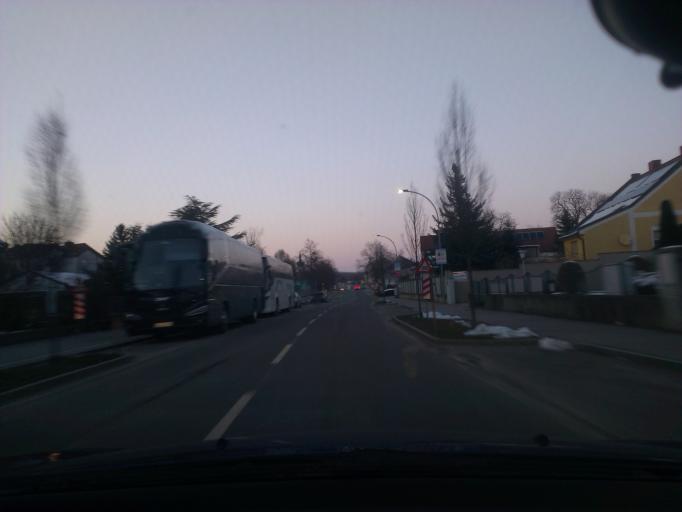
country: AT
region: Lower Austria
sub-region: Politischer Bezirk Wien-Umgebung
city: Fischamend Dorf
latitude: 48.1148
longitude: 16.6140
